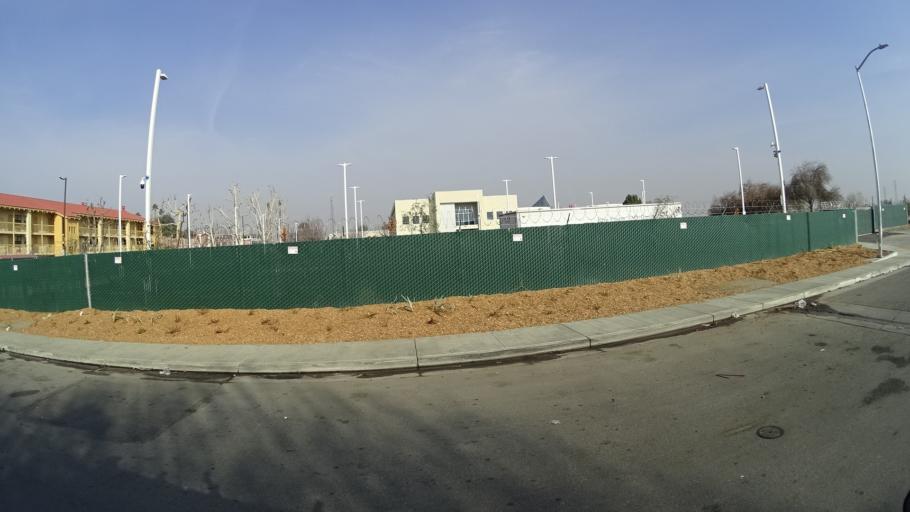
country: US
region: California
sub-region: Kern County
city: Bakersfield
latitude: 35.3831
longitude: -119.0409
